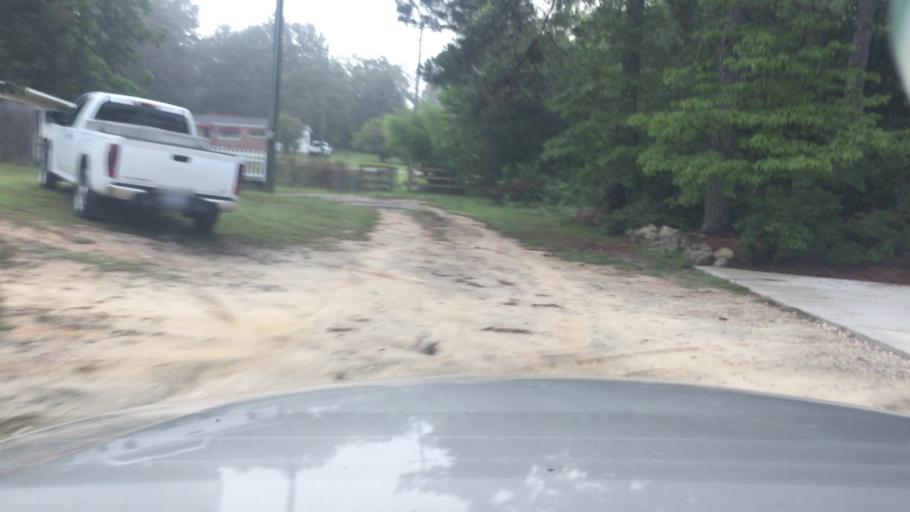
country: US
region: North Carolina
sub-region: Cumberland County
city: Hope Mills
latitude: 35.0174
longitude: -78.9397
